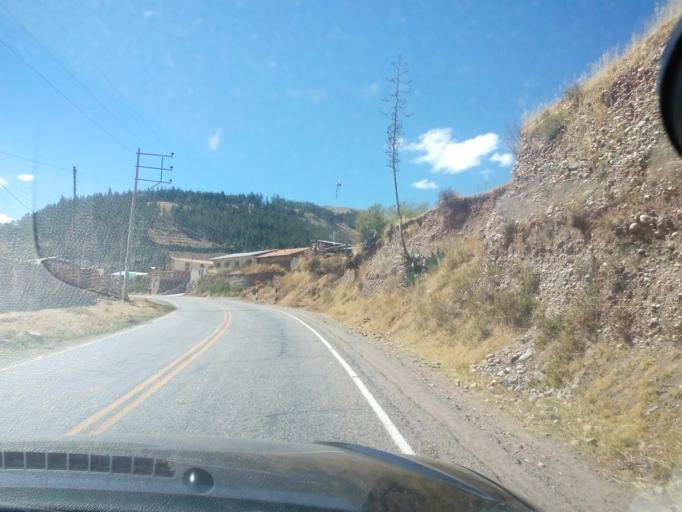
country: PE
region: Cusco
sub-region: Provincia de Canchis
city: Combapata
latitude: -14.0998
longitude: -71.4339
